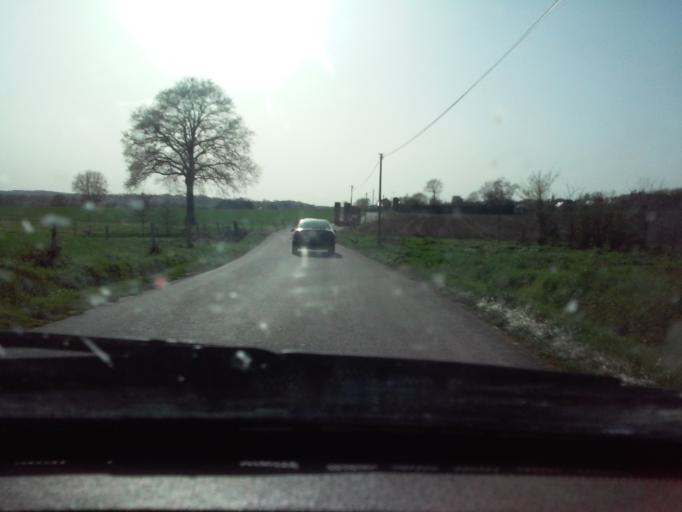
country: FR
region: Brittany
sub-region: Departement d'Ille-et-Vilaine
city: Saint-Jean-sur-Couesnon
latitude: 48.3005
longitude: -1.3465
